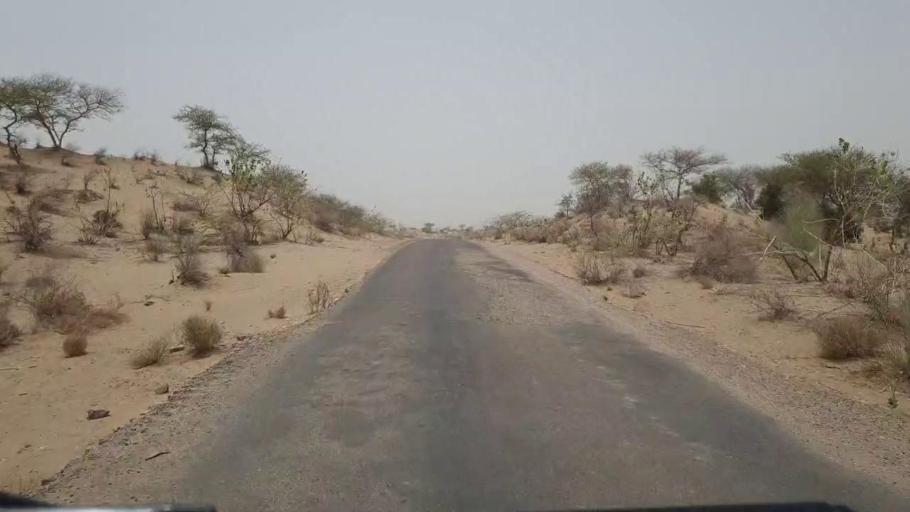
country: PK
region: Sindh
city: Naukot
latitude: 24.7748
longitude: 69.5369
